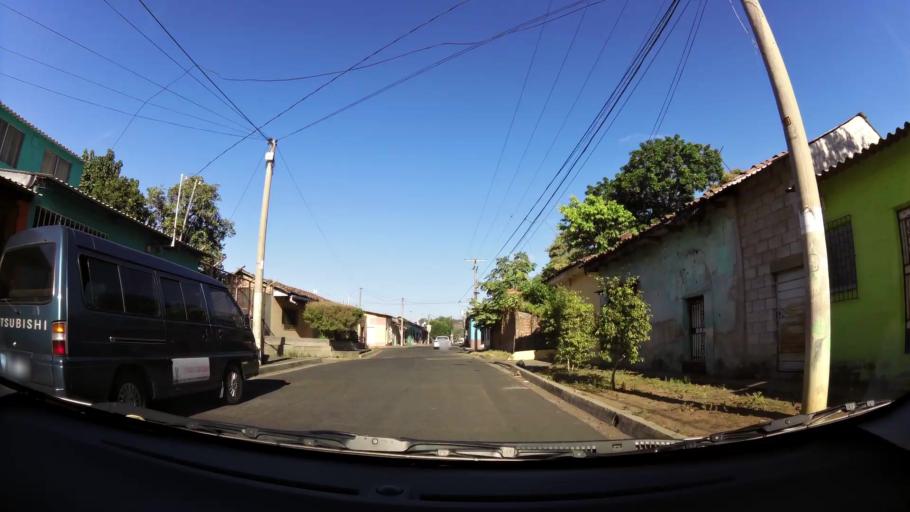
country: SV
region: Sonsonate
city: Sonsonate
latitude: 13.7176
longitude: -89.7200
